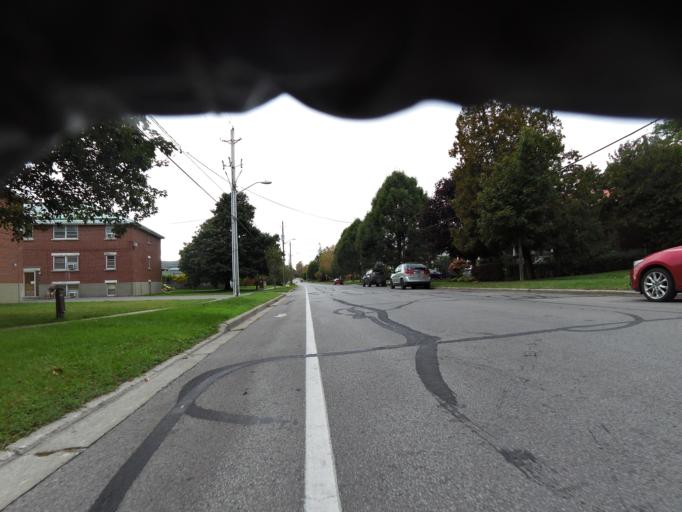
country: CA
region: Ontario
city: Cobourg
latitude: 43.9591
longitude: -78.1771
